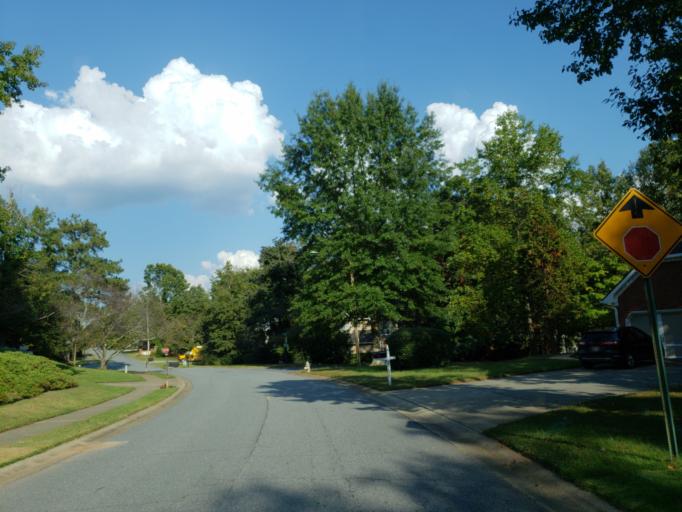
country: US
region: Georgia
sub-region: Cherokee County
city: Woodstock
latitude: 34.0590
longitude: -84.4466
